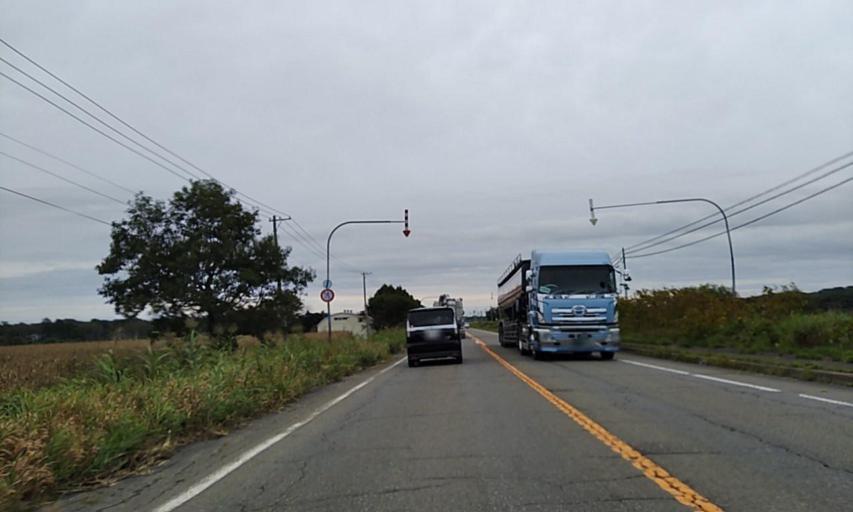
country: JP
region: Hokkaido
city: Obihiro
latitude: 42.4631
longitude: 143.2792
